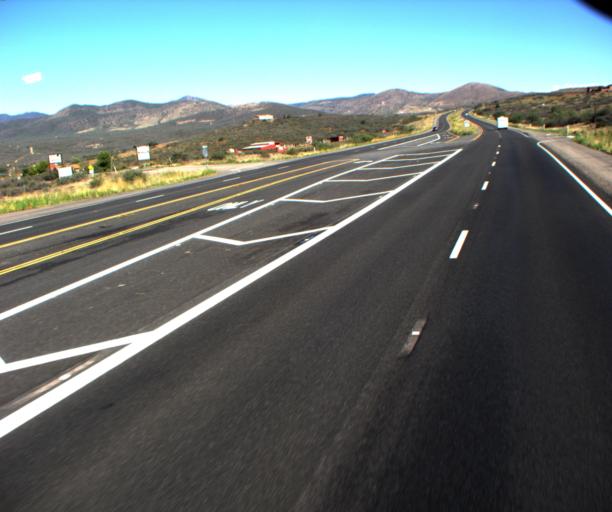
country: US
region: Arizona
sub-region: Yavapai County
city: Mayer
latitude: 34.4283
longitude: -112.2551
